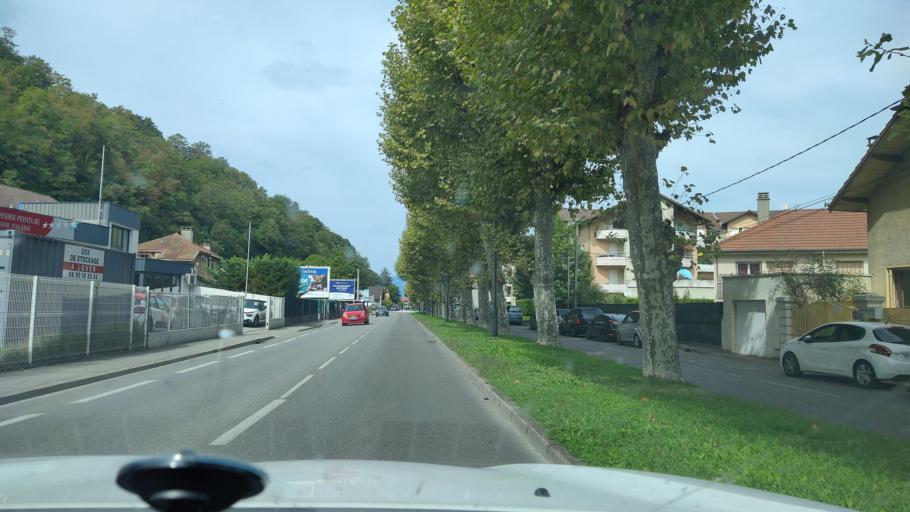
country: FR
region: Rhone-Alpes
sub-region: Departement de la Savoie
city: Tresserve
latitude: 45.6902
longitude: 5.9032
